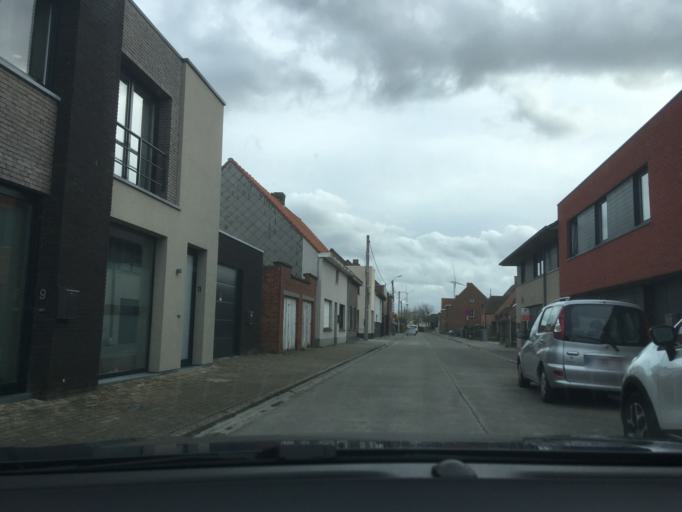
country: BE
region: Flanders
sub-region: Provincie West-Vlaanderen
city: Wielsbeke
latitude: 50.9085
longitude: 3.3661
